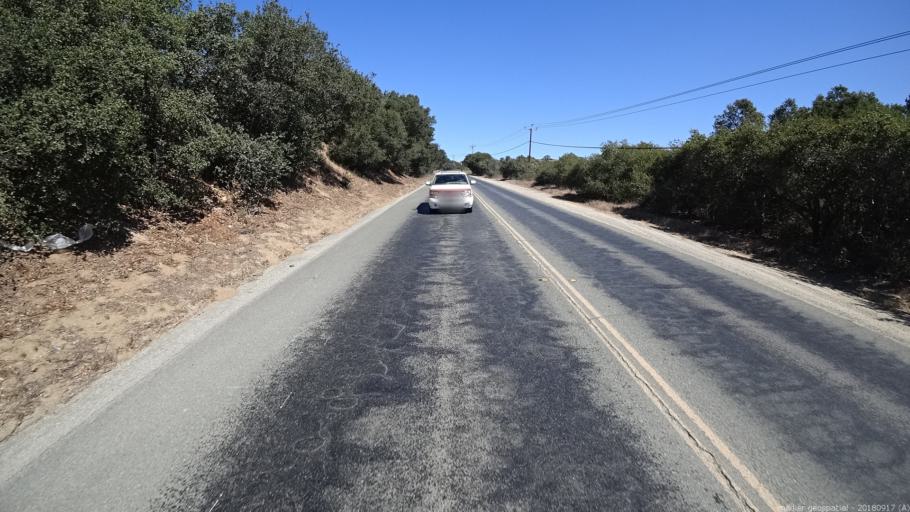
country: US
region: California
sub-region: Monterey County
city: Prunedale
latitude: 36.8007
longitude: -121.6155
